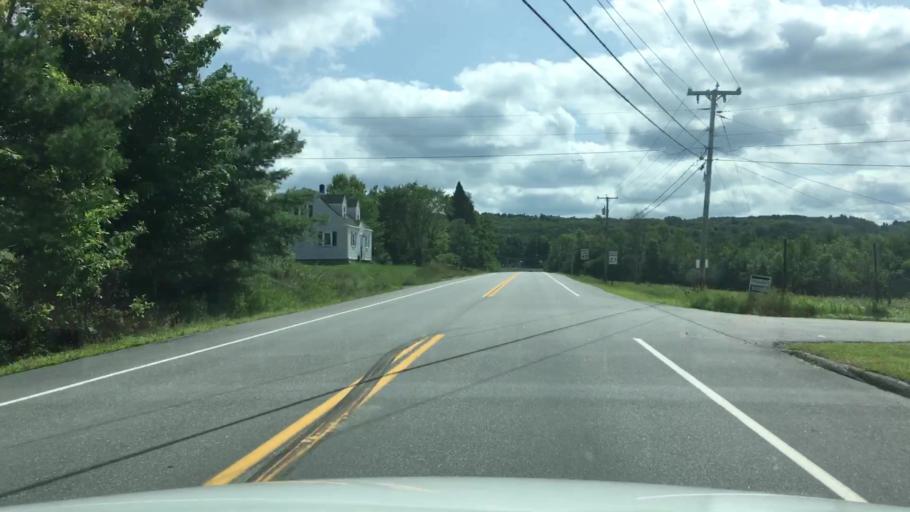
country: US
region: Maine
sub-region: Kennebec County
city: Pittston
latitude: 44.1927
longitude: -69.7486
